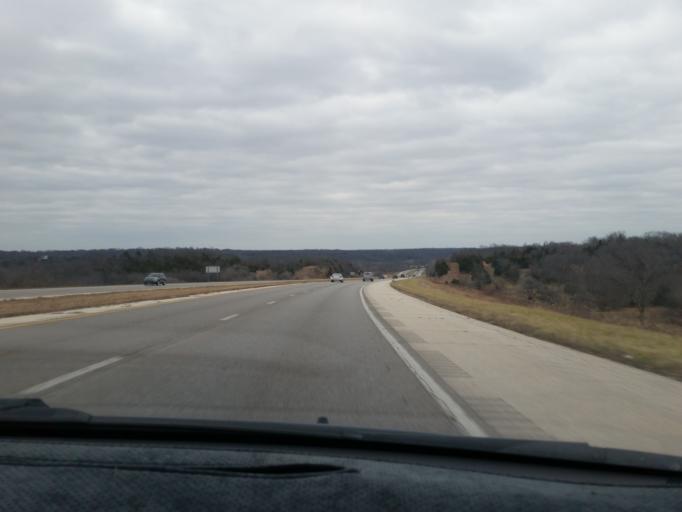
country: US
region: Kansas
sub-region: Johnson County
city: De Soto
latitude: 38.9600
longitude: -94.9329
